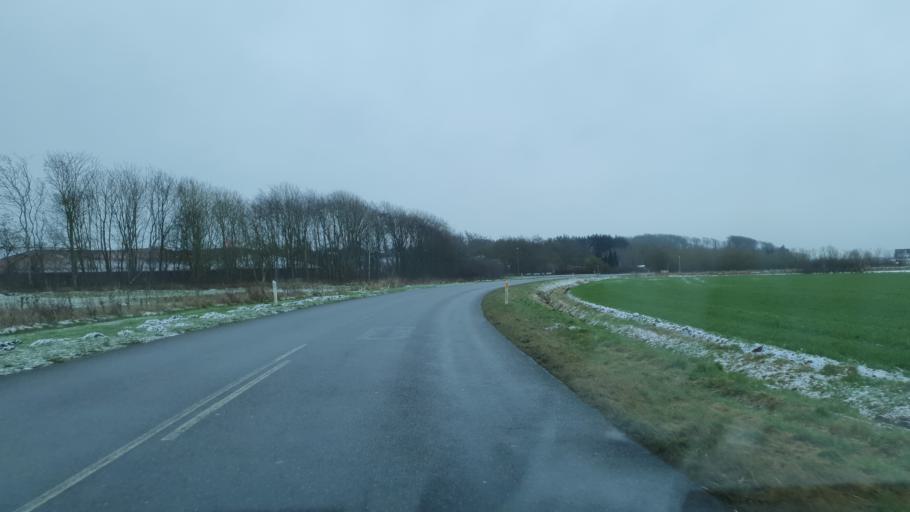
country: DK
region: North Denmark
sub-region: Jammerbugt Kommune
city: Brovst
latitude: 57.1004
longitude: 9.5078
